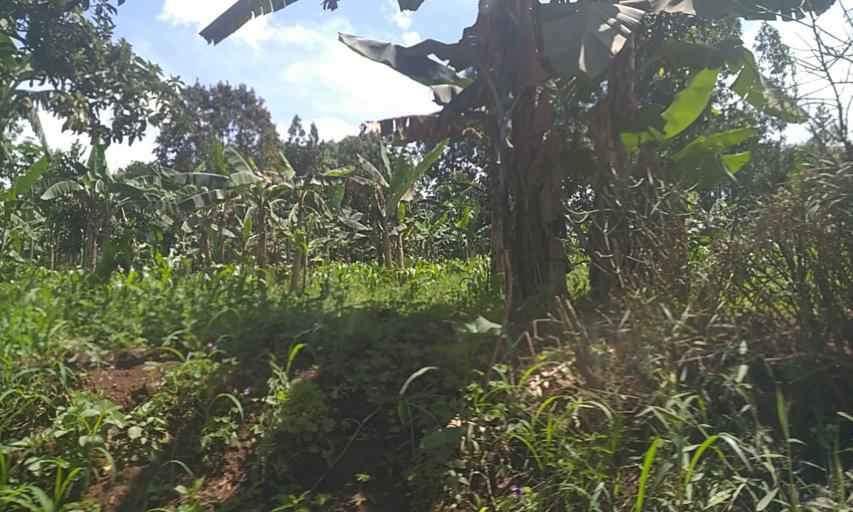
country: UG
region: Central Region
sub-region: Wakiso District
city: Wakiso
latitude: 0.4103
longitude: 32.4739
